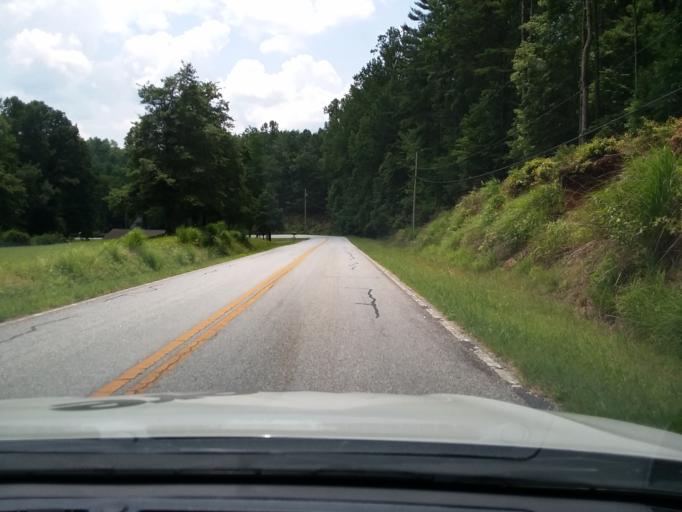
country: US
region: Georgia
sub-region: Rabun County
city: Mountain City
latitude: 34.9665
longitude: -83.1864
